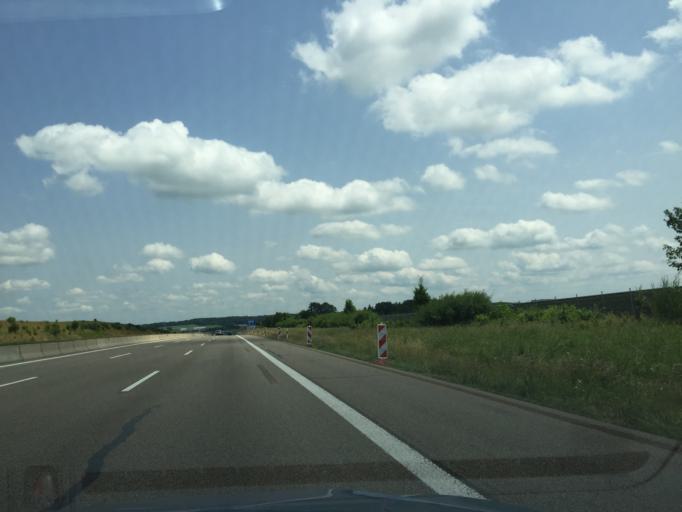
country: DE
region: Bavaria
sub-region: Swabia
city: Wasserburg
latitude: 48.4296
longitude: 10.2638
